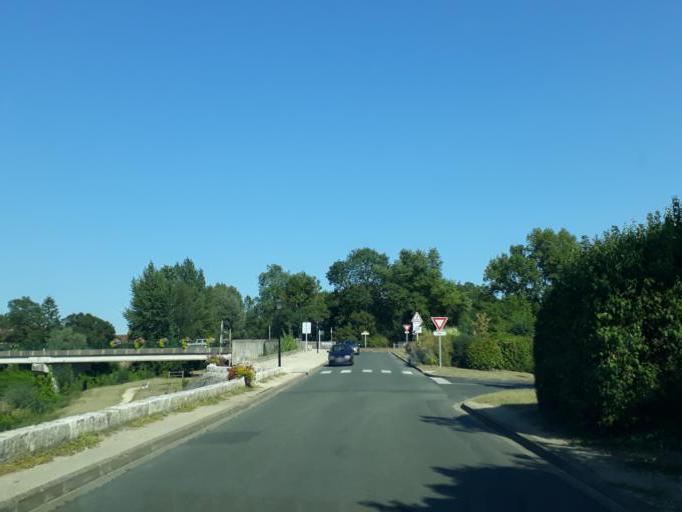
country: FR
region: Centre
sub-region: Departement du Loir-et-Cher
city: Selles-sur-Cher
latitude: 47.2775
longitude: 1.5566
